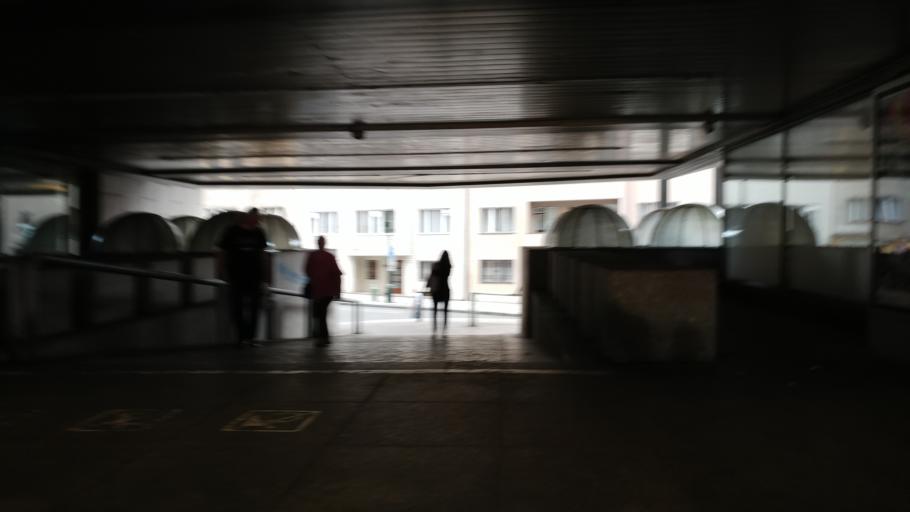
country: CZ
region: Praha
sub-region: Praha 1
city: Stare Mesto
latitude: 50.0807
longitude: 14.4142
